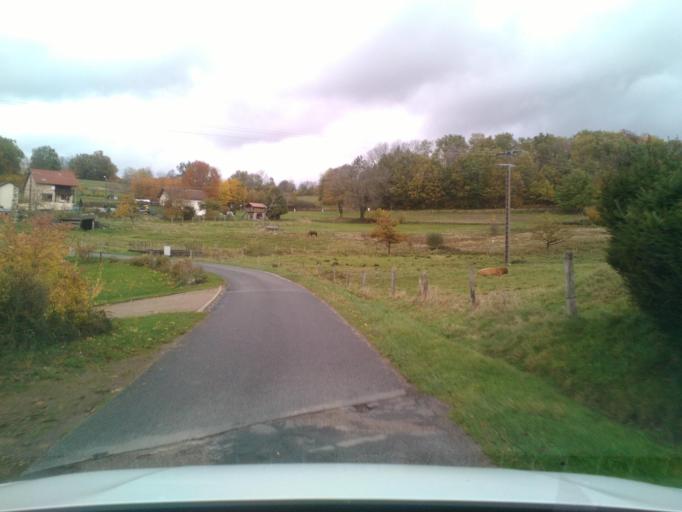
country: FR
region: Lorraine
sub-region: Departement des Vosges
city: Senones
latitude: 48.3425
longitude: 7.0163
